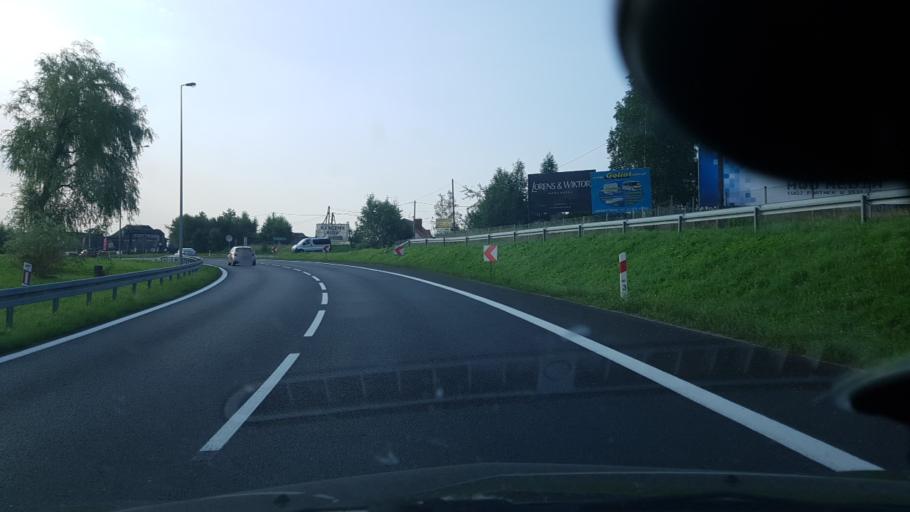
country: PL
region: Lesser Poland Voivodeship
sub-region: Powiat myslenicki
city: Beczarka
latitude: 49.8798
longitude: 19.8779
